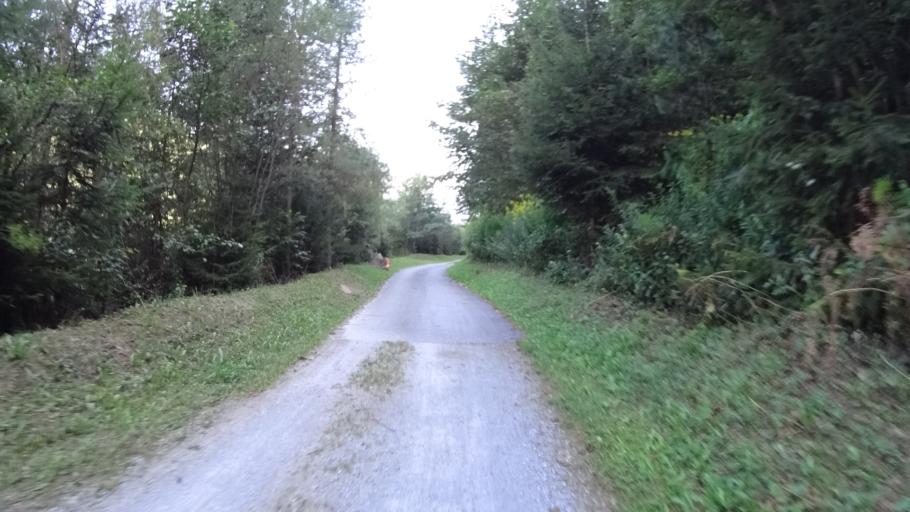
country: AT
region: Carinthia
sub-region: Politischer Bezirk Villach Land
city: Rosegg
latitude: 46.5785
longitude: 14.0192
